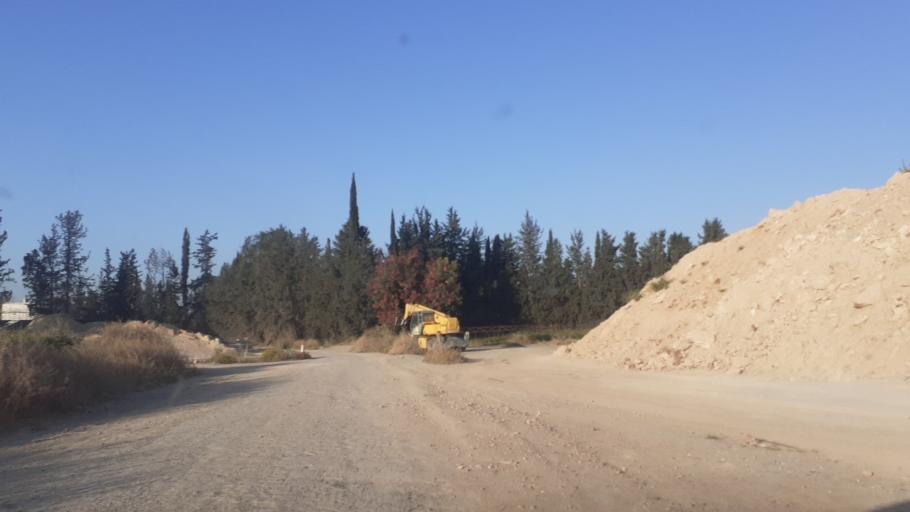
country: CY
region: Limassol
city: Ypsonas
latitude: 34.6673
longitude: 32.9846
